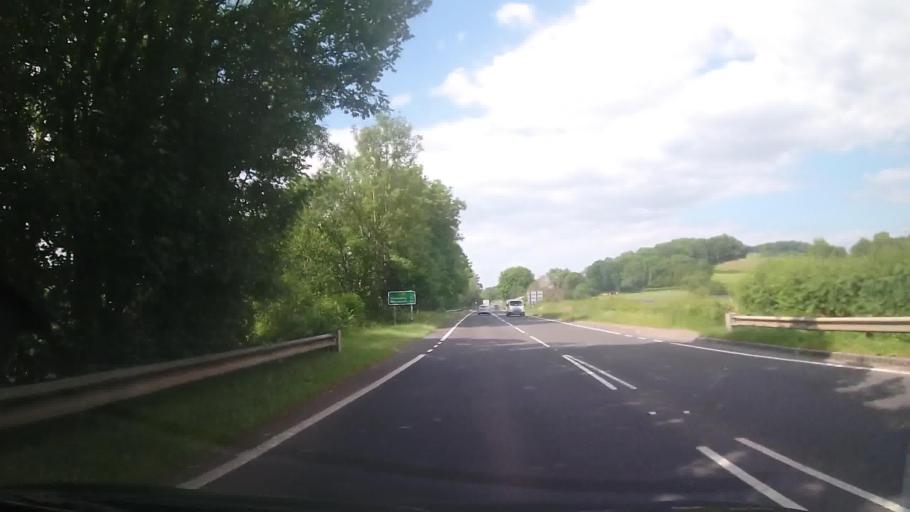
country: GB
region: England
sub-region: Shropshire
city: Ludlow
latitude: 52.3394
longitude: -2.7119
